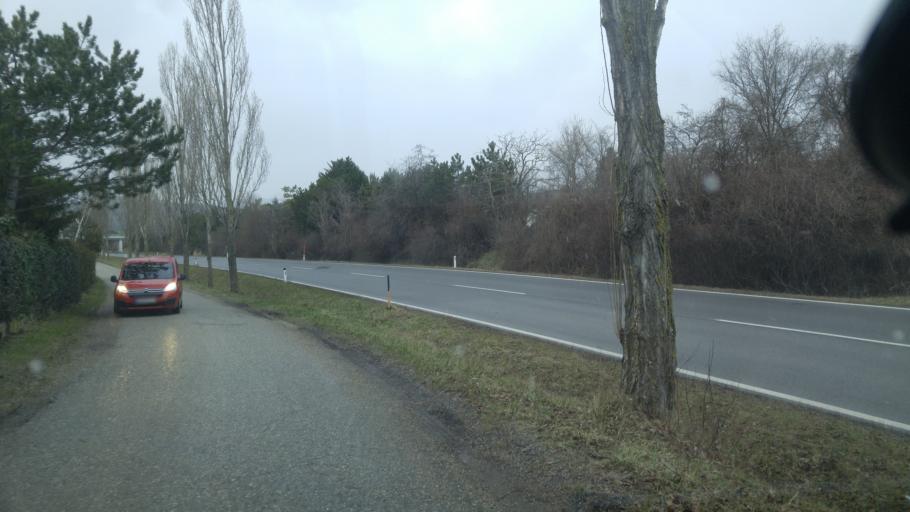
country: AT
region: Lower Austria
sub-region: Politischer Bezirk Baden
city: Baden
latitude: 47.9972
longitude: 16.2216
